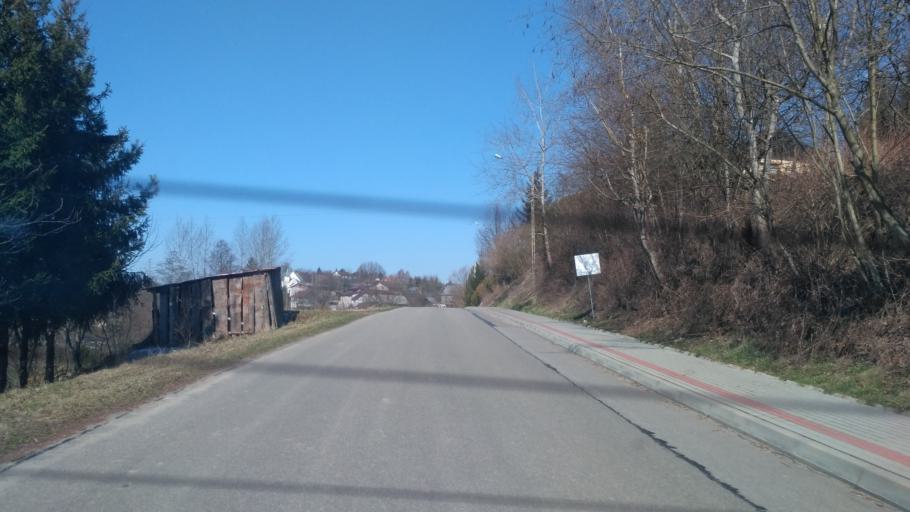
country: PL
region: Subcarpathian Voivodeship
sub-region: Powiat strzyzowski
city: Gwoznica Gorna
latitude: 49.8132
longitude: 22.0372
